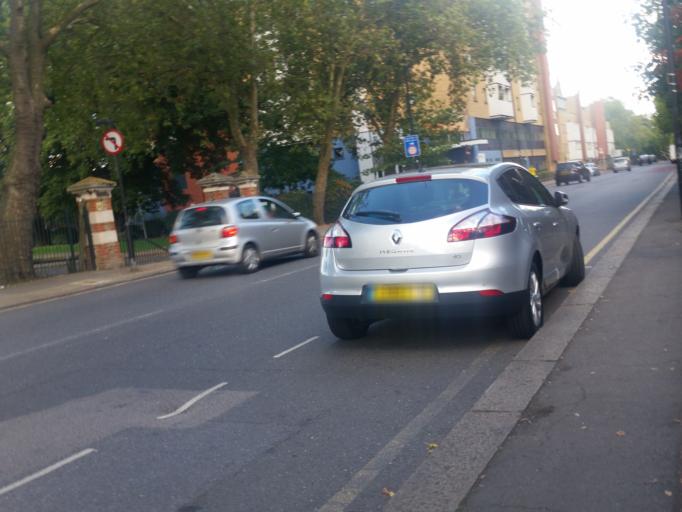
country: GB
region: England
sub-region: Greater London
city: Harringay
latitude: 51.5813
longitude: -0.0887
